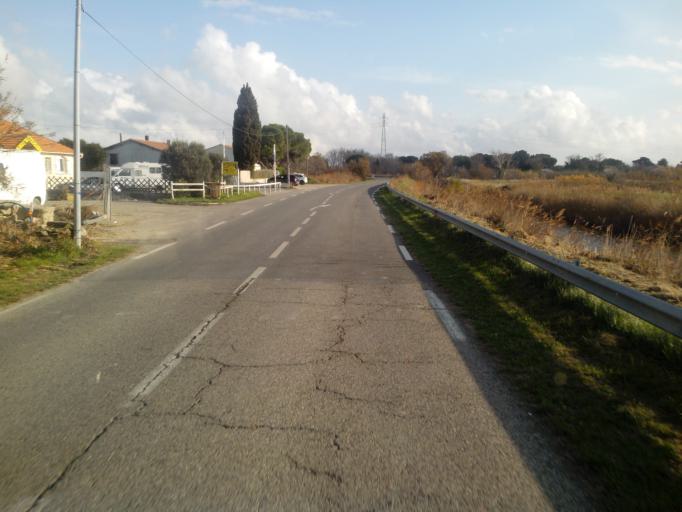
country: FR
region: Provence-Alpes-Cote d'Azur
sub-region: Departement des Bouches-du-Rhone
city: Port-Saint-Louis-du-Rhone
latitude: 43.4218
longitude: 4.7299
